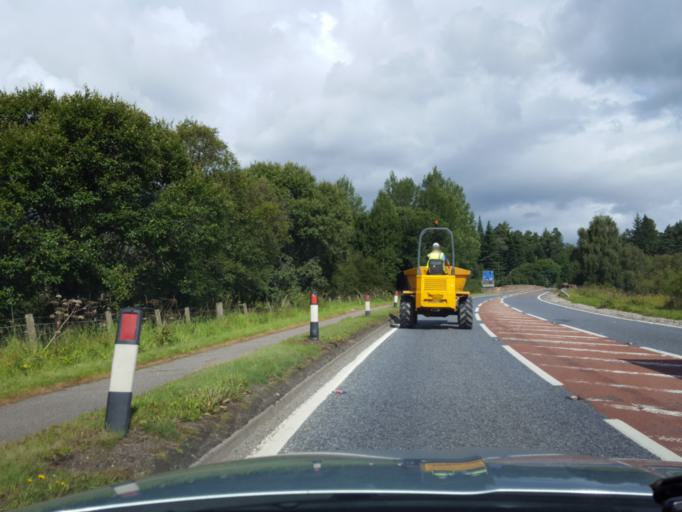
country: GB
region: Scotland
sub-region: Highland
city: Grantown on Spey
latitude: 57.3199
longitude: -3.6057
